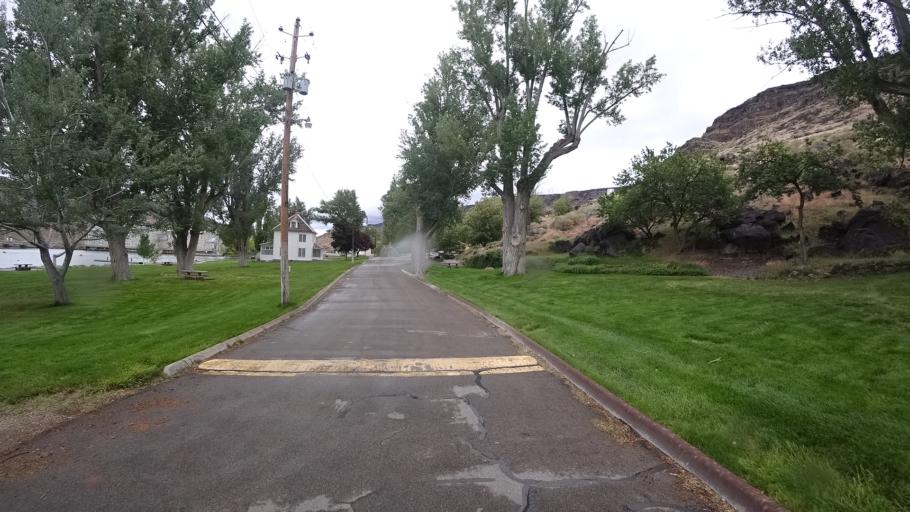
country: US
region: Idaho
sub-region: Owyhee County
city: Murphy
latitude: 43.2423
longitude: -116.3757
